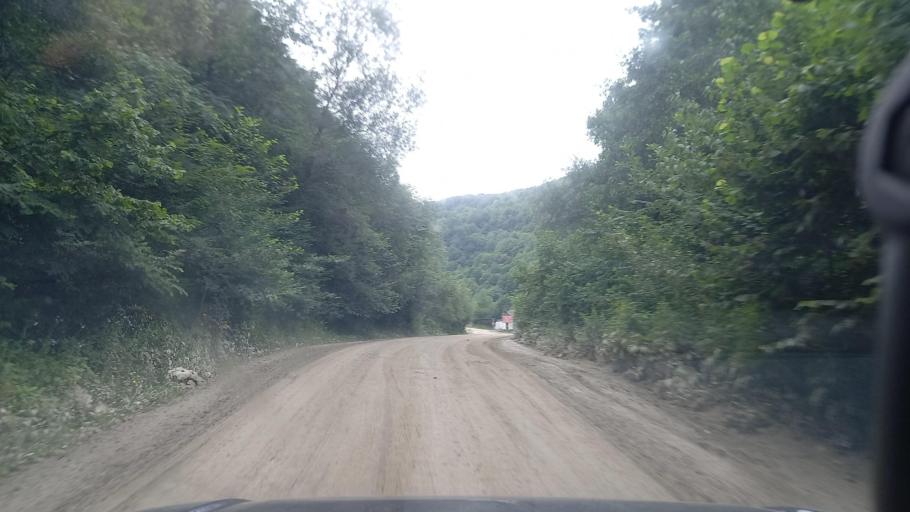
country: RU
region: Karachayevo-Cherkesiya
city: Kurdzhinovo
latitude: 43.9448
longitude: 40.9583
